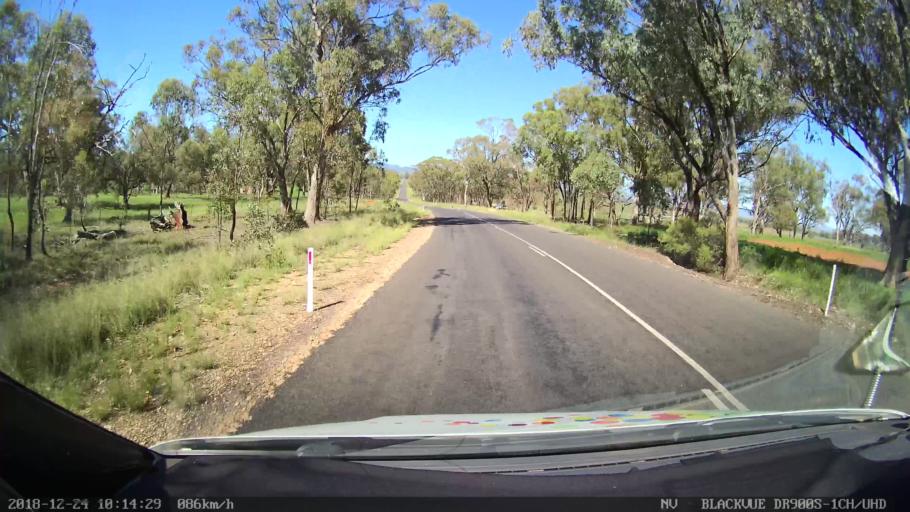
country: AU
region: New South Wales
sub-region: Liverpool Plains
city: Quirindi
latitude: -31.6978
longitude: 150.6275
